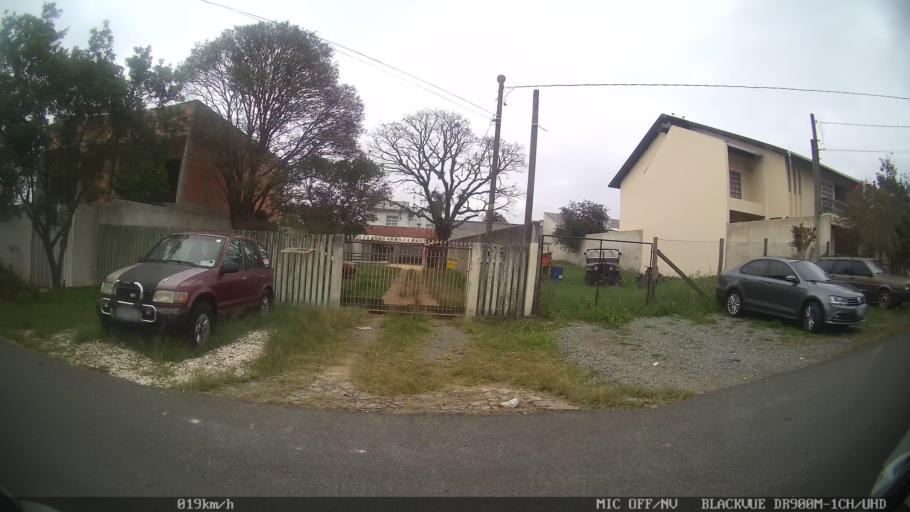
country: BR
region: Parana
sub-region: Almirante Tamandare
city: Almirante Tamandare
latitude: -25.3792
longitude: -49.3309
